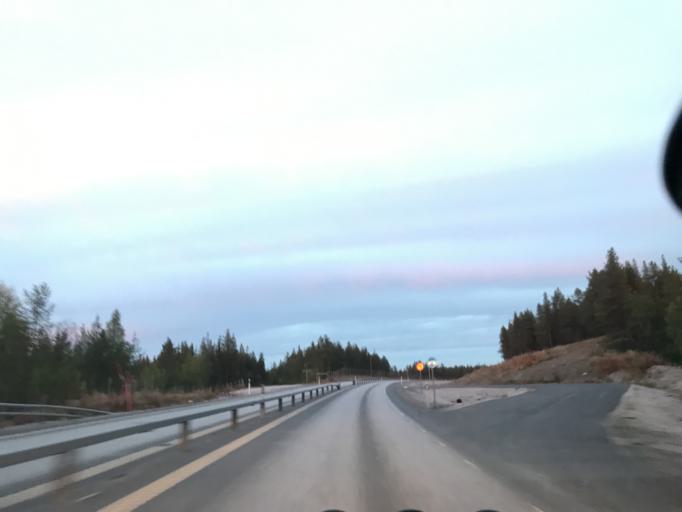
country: SE
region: Norrbotten
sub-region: Gallivare Kommun
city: Malmberget
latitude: 67.6663
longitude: 20.9779
